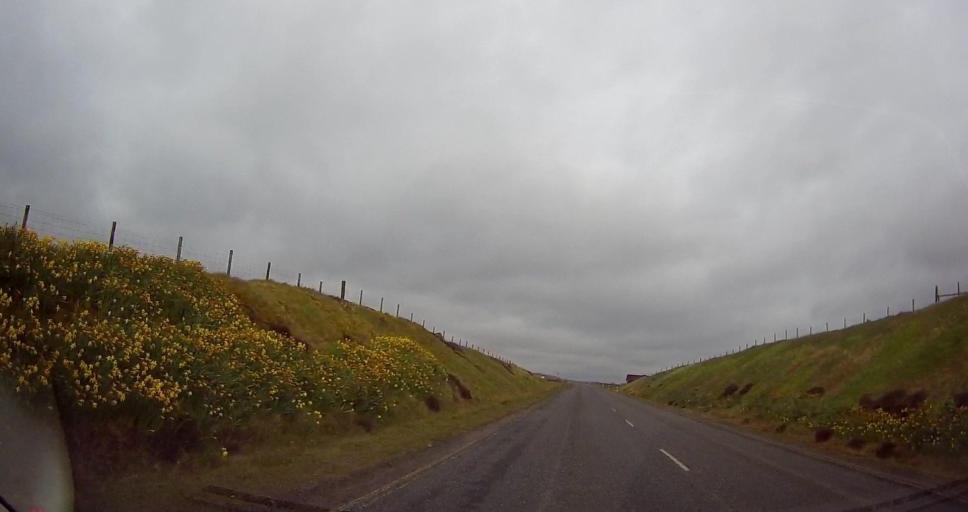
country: GB
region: Scotland
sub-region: Shetland Islands
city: Lerwick
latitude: 60.3754
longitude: -1.3382
